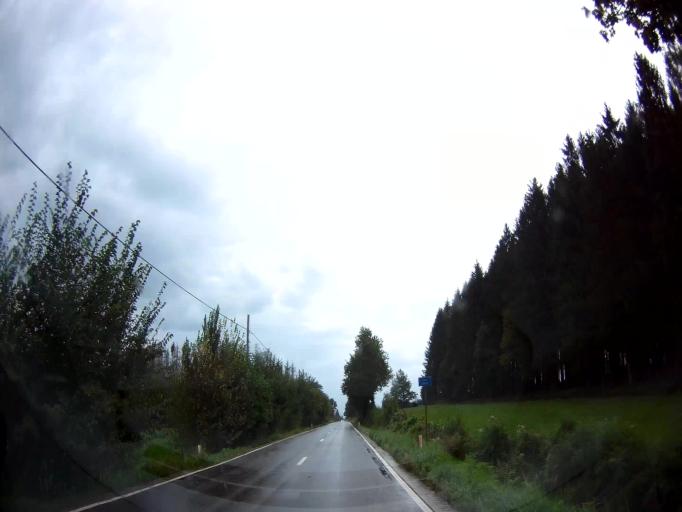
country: BE
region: Wallonia
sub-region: Province de Liege
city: Ferrieres
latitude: 50.4315
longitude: 5.6055
